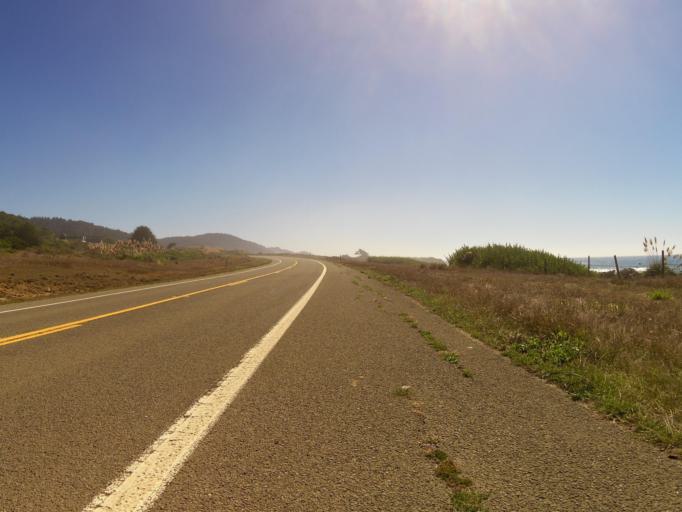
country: US
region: California
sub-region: Mendocino County
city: Fort Bragg
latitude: 39.6717
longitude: -123.7910
